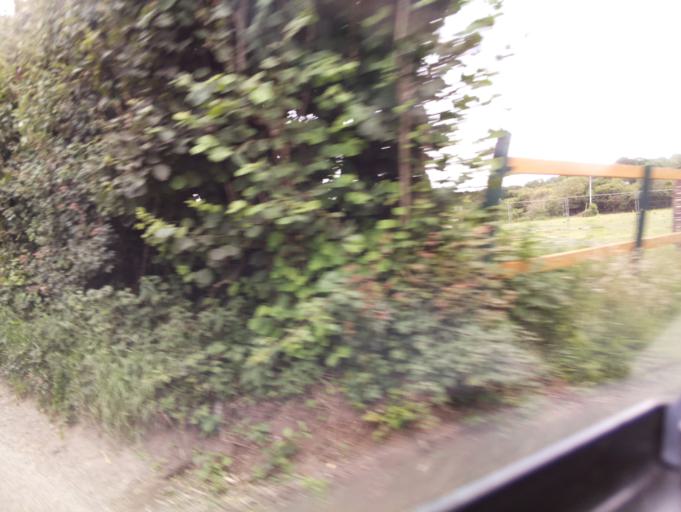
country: GB
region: England
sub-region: Somerset
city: Bradley Cross
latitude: 51.2622
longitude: -2.7595
